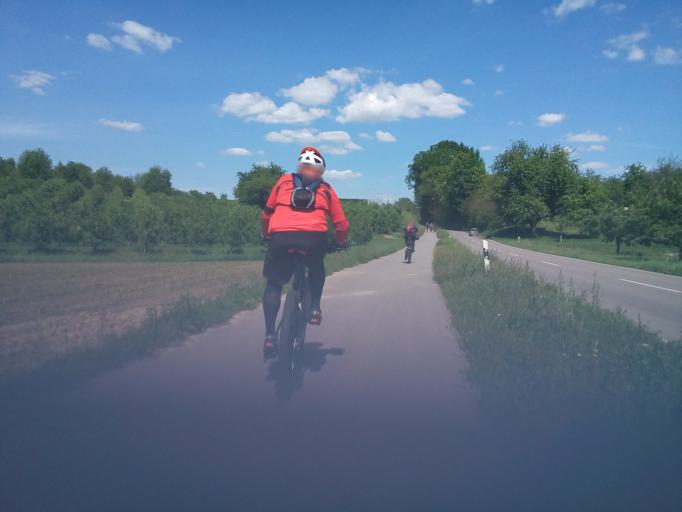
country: DE
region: Baden-Wuerttemberg
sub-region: Freiburg Region
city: Haslach
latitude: 48.5761
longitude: 8.0408
